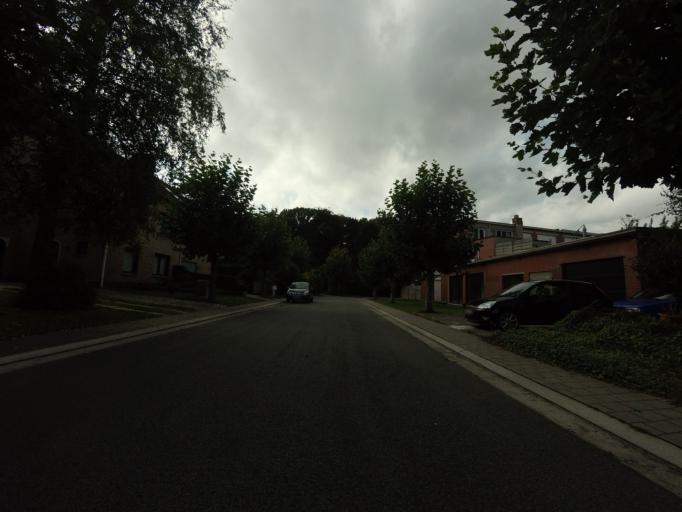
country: BE
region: Flanders
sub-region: Provincie Antwerpen
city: Boom
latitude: 51.1140
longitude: 4.3760
